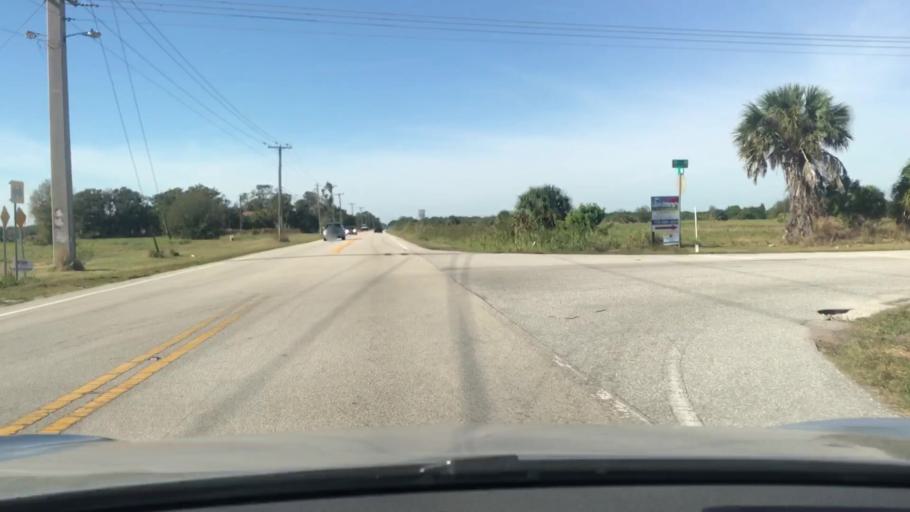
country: US
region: Florida
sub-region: Indian River County
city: Winter Beach
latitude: 27.7478
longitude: -80.4693
